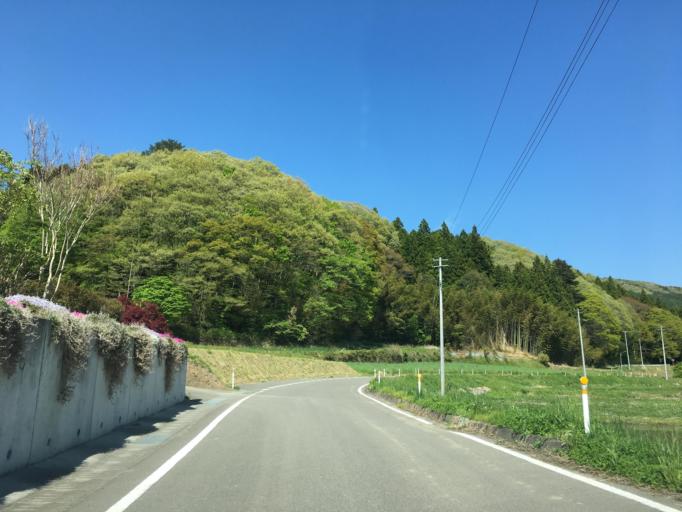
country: JP
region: Fukushima
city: Funehikimachi-funehiki
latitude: 37.3023
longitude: 140.6680
